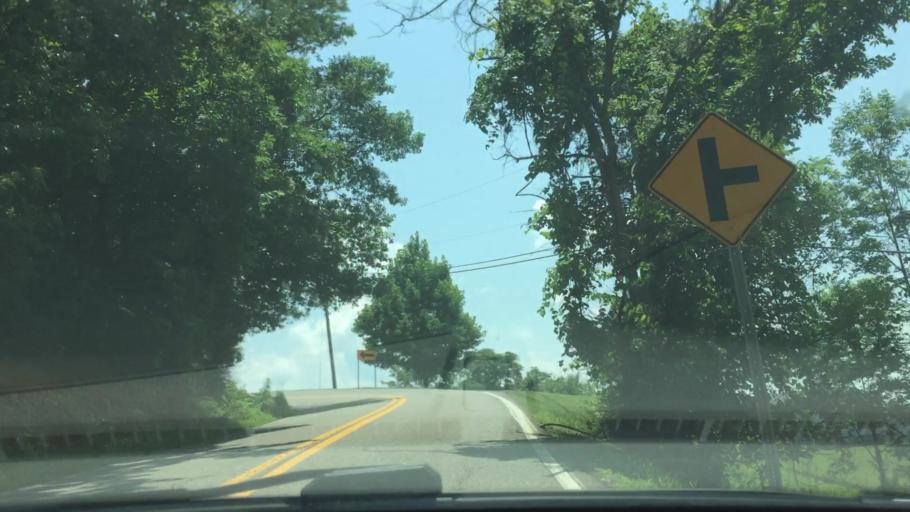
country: US
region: West Virginia
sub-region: Wetzel County
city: New Martinsville
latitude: 39.7007
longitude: -80.7580
